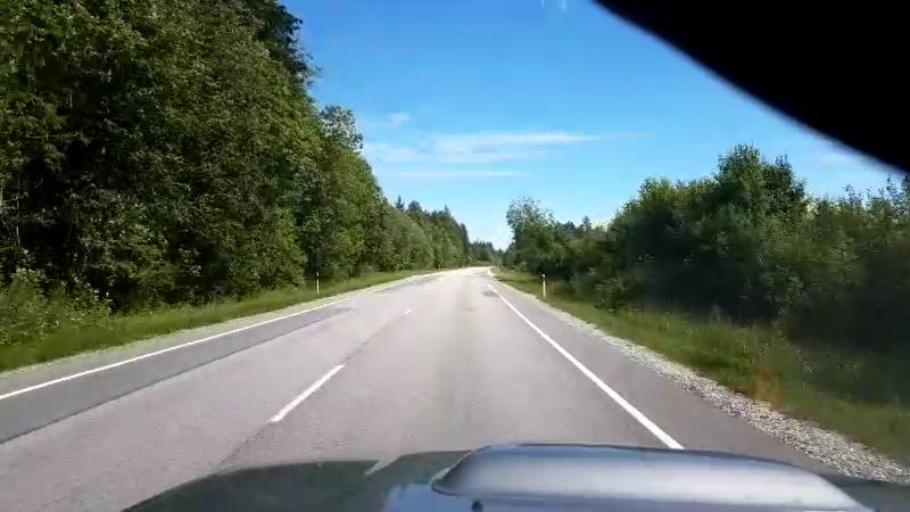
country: EE
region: Jaervamaa
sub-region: Koeru vald
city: Koeru
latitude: 58.9734
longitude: 26.1233
